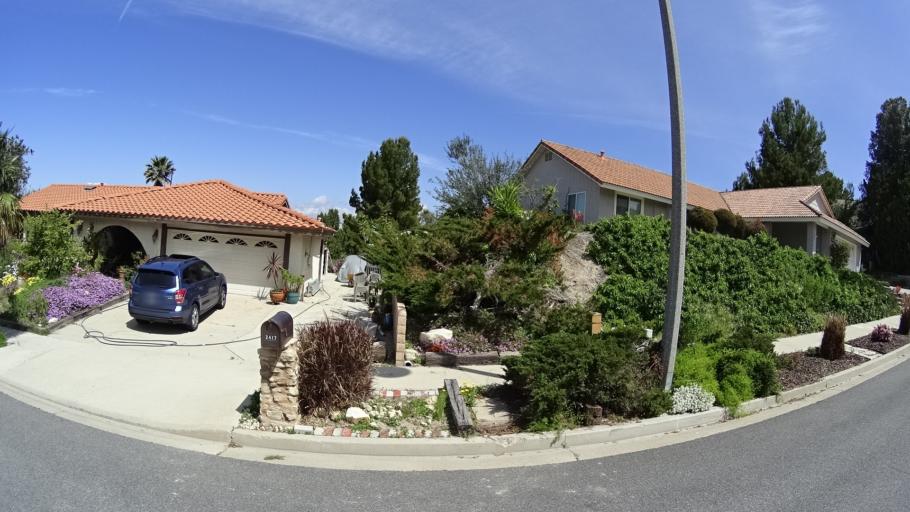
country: US
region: California
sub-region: Ventura County
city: Thousand Oaks
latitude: 34.2271
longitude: -118.8344
